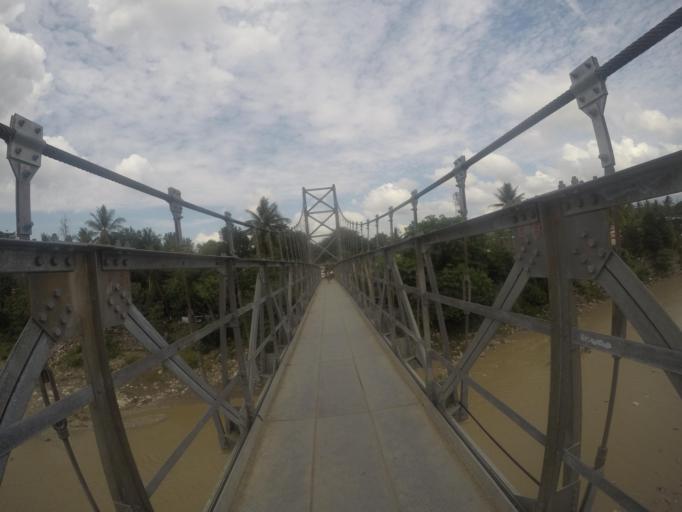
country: TL
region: Viqueque
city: Viqueque
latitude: -8.8601
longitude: 126.3655
